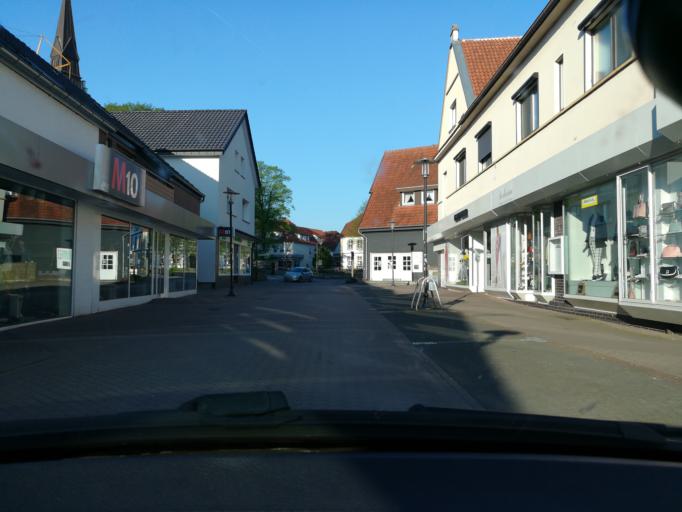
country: DE
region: North Rhine-Westphalia
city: Versmold
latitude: 52.0397
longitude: 8.1536
